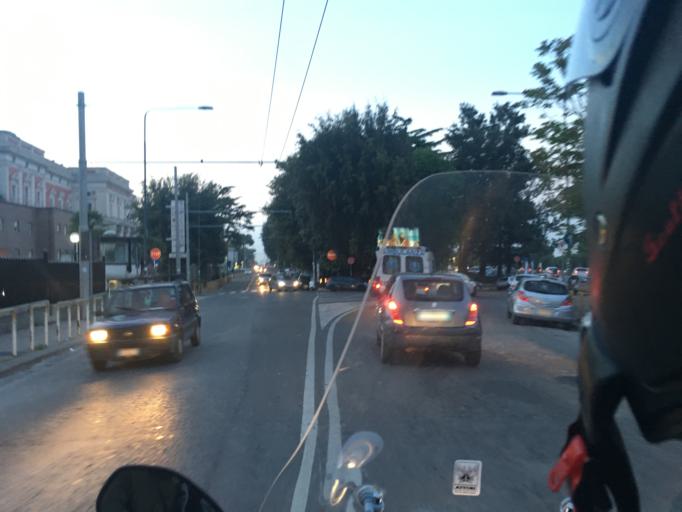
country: IT
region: Campania
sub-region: Provincia di Napoli
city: Napoli
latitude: 40.8634
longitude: 14.2259
